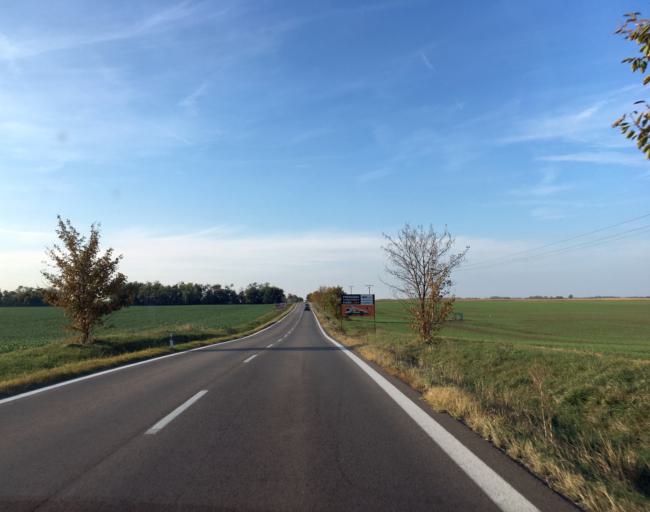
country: SK
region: Nitriansky
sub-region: Okres Nove Zamky
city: Nove Zamky
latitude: 48.0231
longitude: 18.1418
